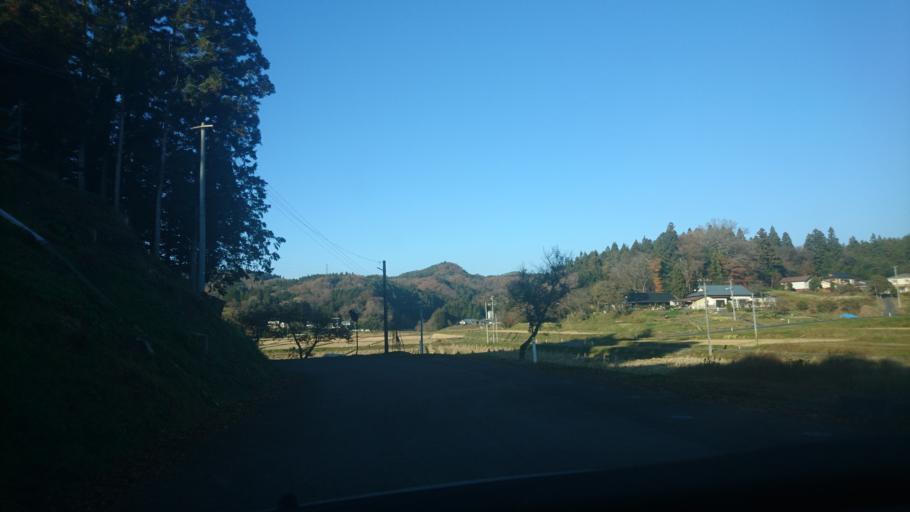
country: JP
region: Iwate
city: Ichinoseki
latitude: 38.9057
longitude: 141.2268
